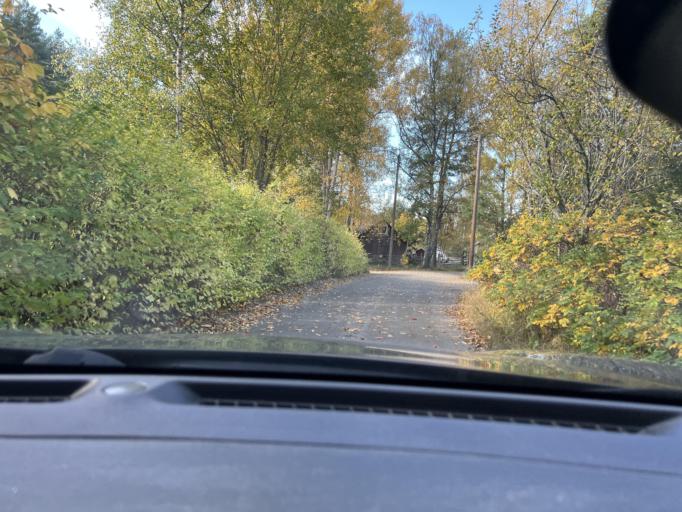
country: SE
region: Stockholm
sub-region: Vallentuna Kommun
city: Vallentuna
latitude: 59.5068
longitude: 18.0923
